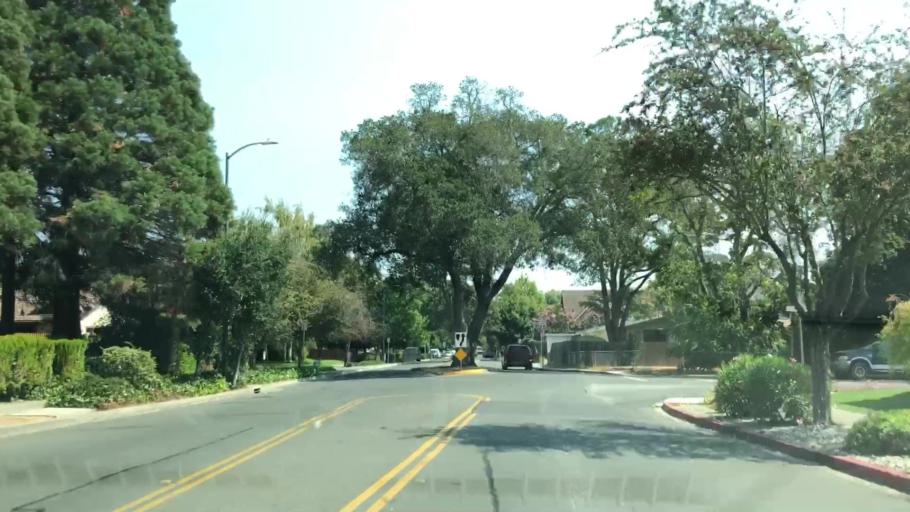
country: US
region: California
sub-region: Napa County
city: Napa
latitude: 38.2987
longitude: -122.2973
